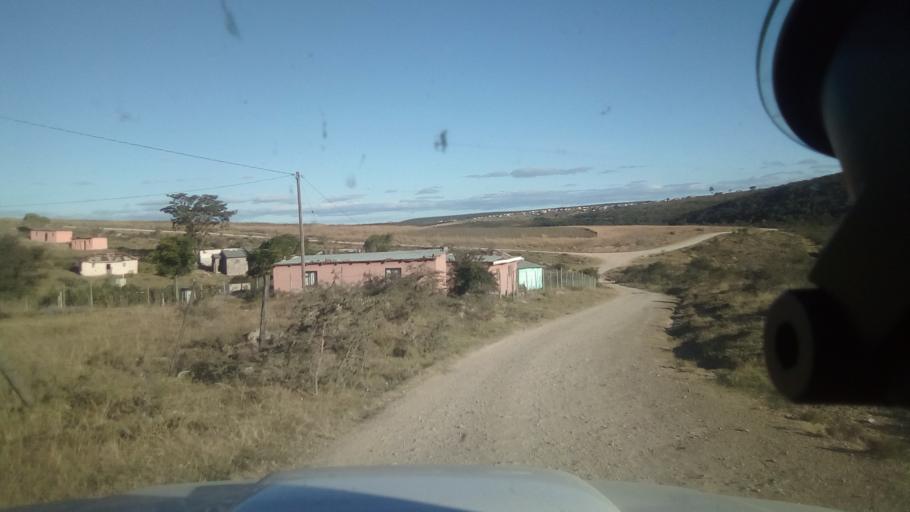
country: ZA
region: Eastern Cape
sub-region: Buffalo City Metropolitan Municipality
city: Bhisho
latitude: -32.7356
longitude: 27.3604
